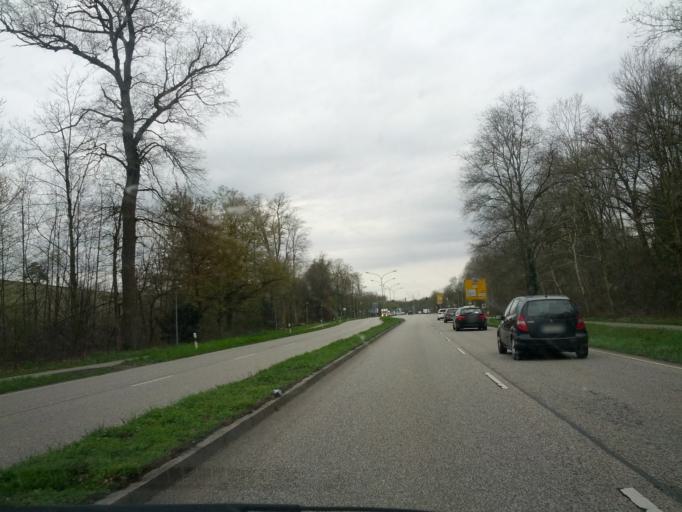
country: DE
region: Baden-Wuerttemberg
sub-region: Freiburg Region
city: Gundelfingen
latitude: 48.0309
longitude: 7.8373
